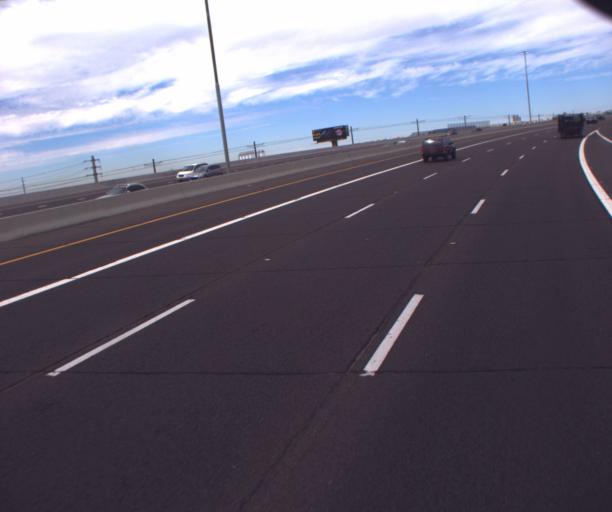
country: US
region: Arizona
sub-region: Maricopa County
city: Tempe Junction
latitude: 33.4408
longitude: -111.9677
